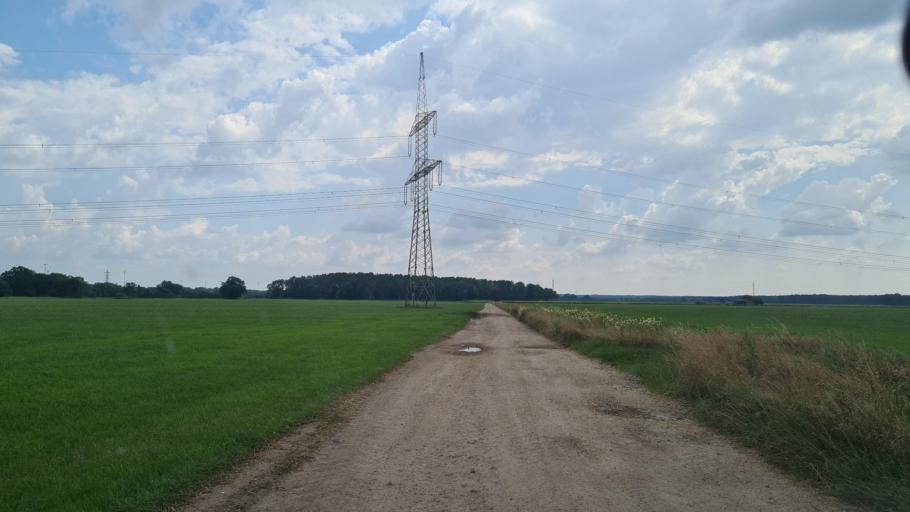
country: DE
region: Brandenburg
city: Sallgast
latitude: 51.6305
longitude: 13.8663
